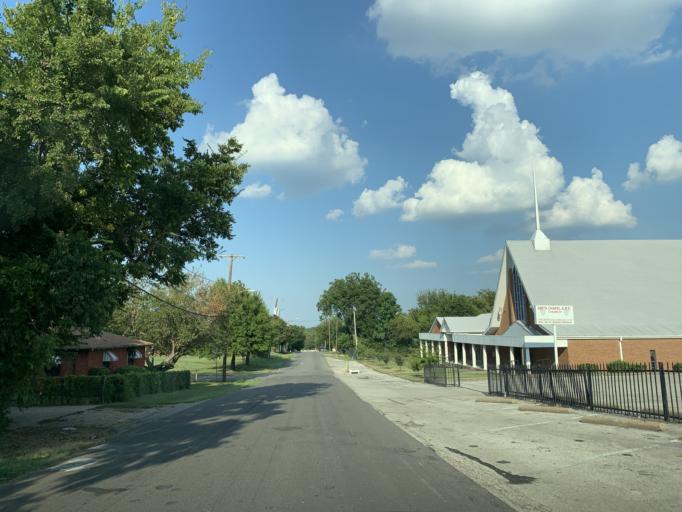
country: US
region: Texas
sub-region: Dallas County
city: Dallas
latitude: 32.7427
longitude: -96.7911
